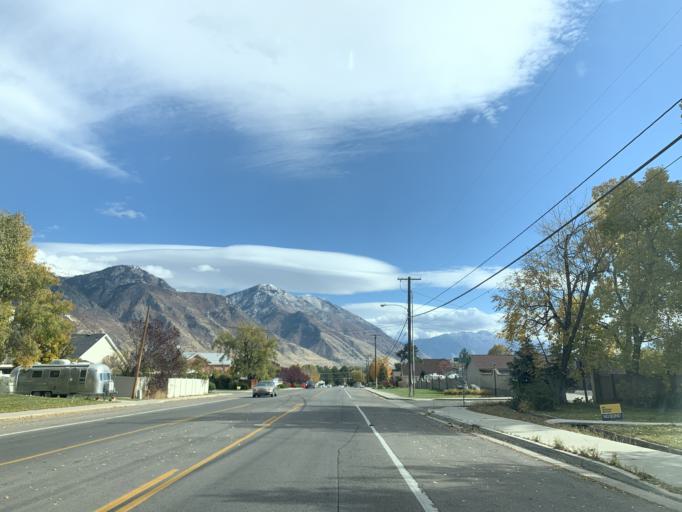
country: US
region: Utah
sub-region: Utah County
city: Provo
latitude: 40.2590
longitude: -111.6786
